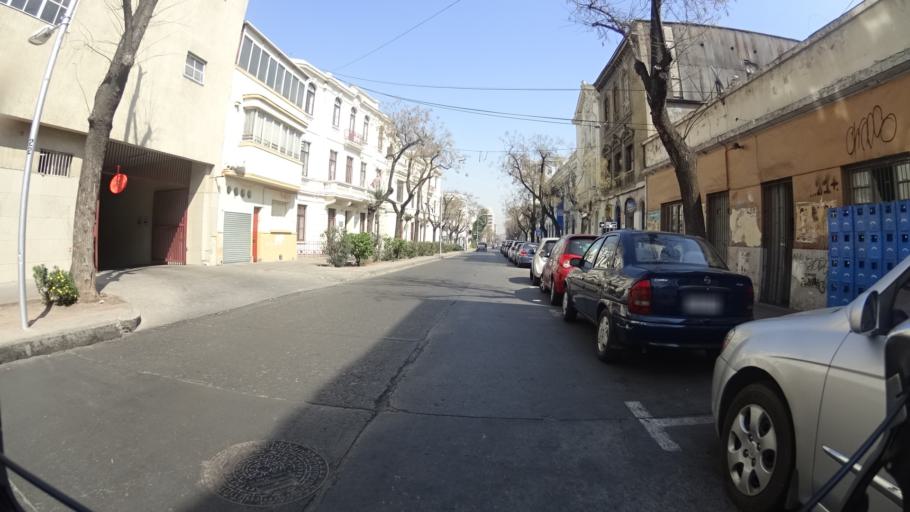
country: CL
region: Santiago Metropolitan
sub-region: Provincia de Santiago
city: Santiago
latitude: -33.4509
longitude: -70.6667
